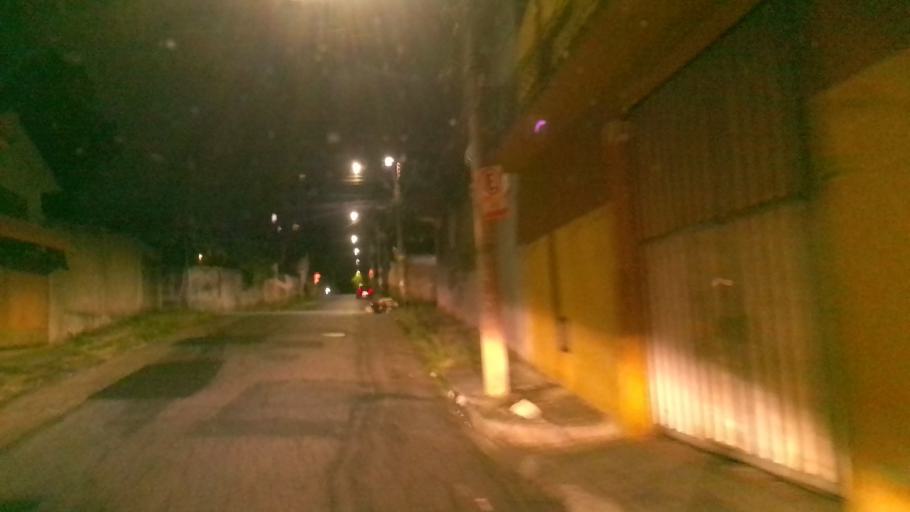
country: BR
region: Minas Gerais
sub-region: Belo Horizonte
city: Belo Horizonte
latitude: -19.9107
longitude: -43.9583
